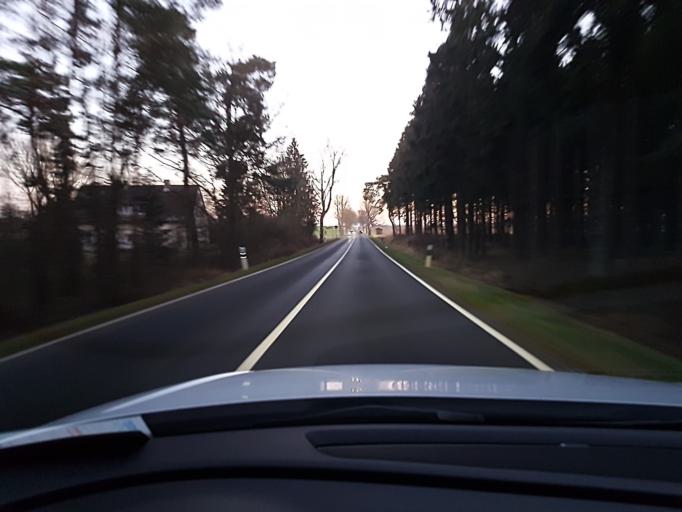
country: DE
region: Mecklenburg-Vorpommern
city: Gingst
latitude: 54.5023
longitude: 13.2785
